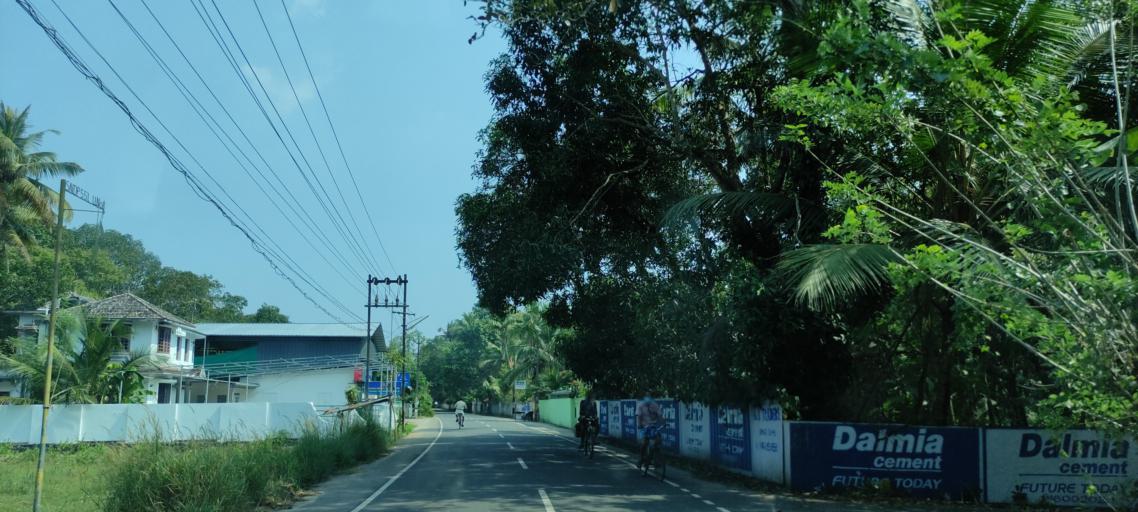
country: IN
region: Kerala
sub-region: Alappuzha
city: Shertallai
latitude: 9.6012
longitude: 76.3247
